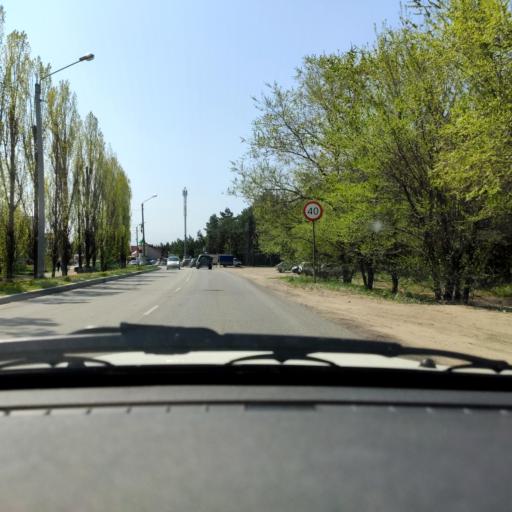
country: RU
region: Voronezj
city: Shilovo
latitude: 51.5538
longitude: 39.0915
